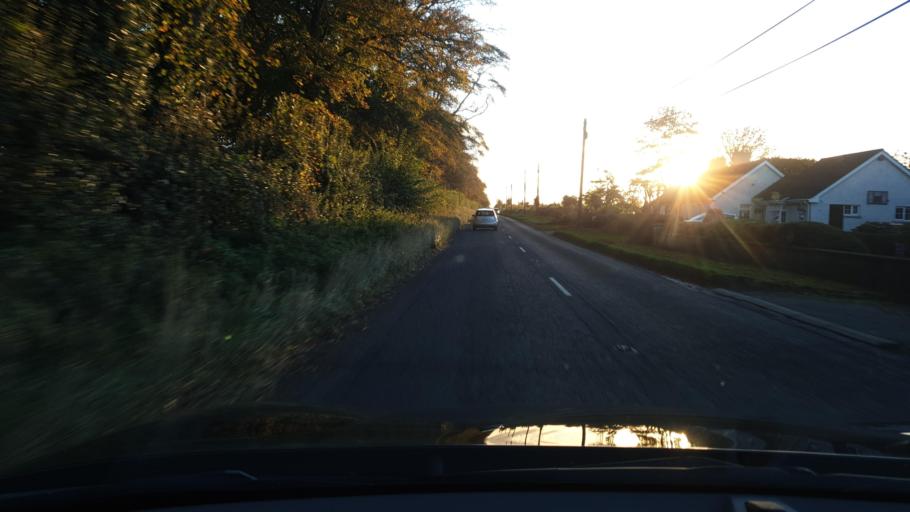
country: IE
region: Leinster
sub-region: Lu
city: Drogheda
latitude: 53.7354
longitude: -6.3119
